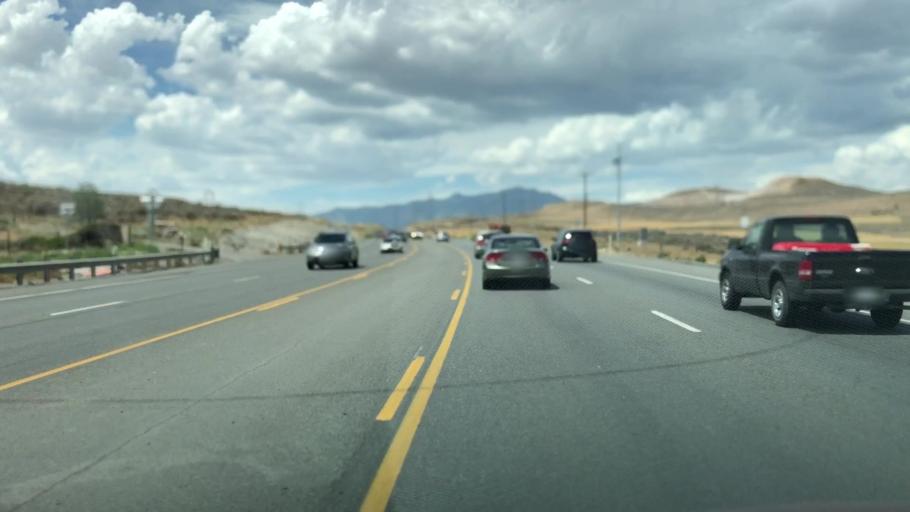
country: US
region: Utah
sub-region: Utah County
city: Saratoga Springs
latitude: 40.3866
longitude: -111.9394
